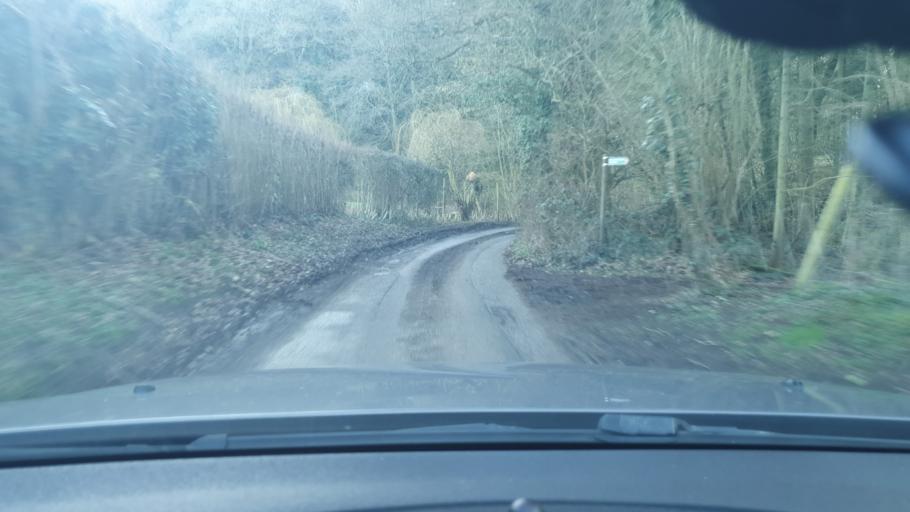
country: GB
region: England
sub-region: Wokingham
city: Wargrave
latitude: 51.5173
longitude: -0.8467
